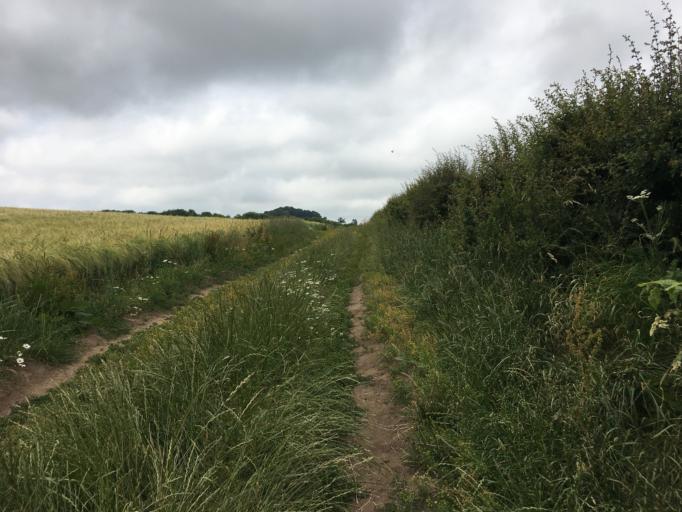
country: GB
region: England
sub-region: Northumberland
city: Belford
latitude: 55.5986
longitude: -1.8399
